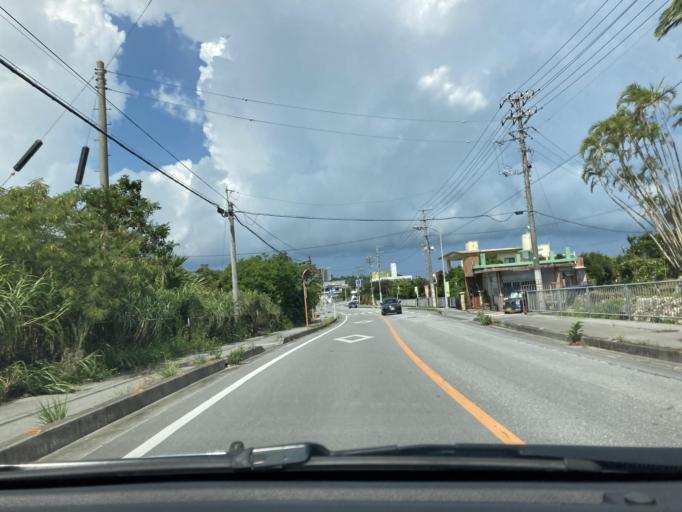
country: JP
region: Okinawa
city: Tomigusuku
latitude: 26.1609
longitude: 127.7762
